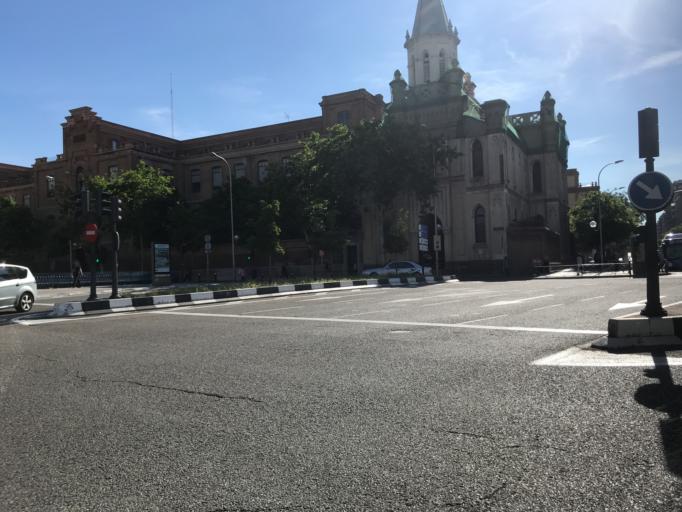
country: ES
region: Madrid
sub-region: Provincia de Madrid
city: Salamanca
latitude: 40.4209
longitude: -3.6688
